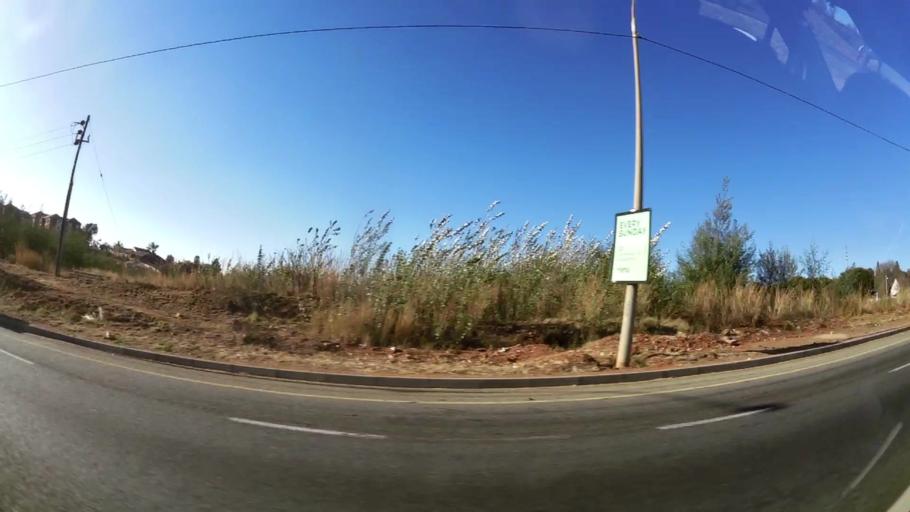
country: ZA
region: Gauteng
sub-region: West Rand District Municipality
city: Krugersdorp
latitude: -26.0763
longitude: 27.7963
